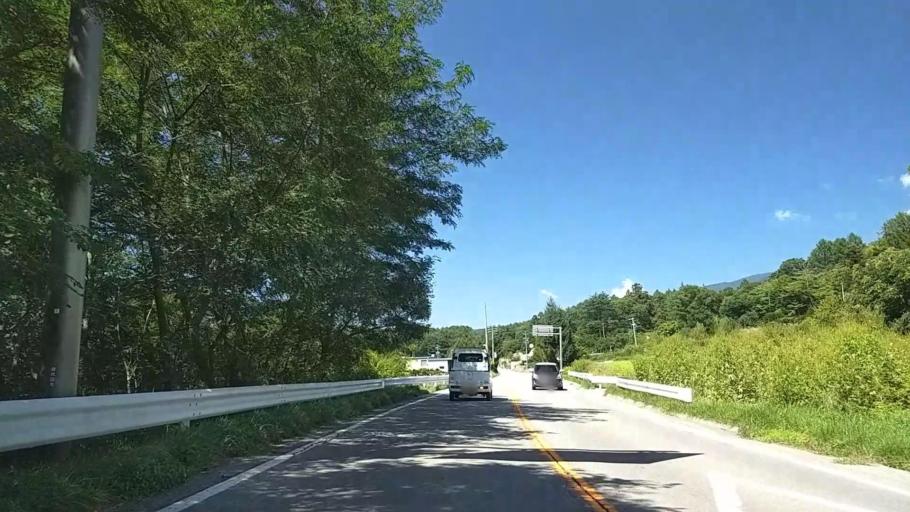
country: JP
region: Nagano
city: Komoro
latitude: 36.3377
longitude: 138.5048
